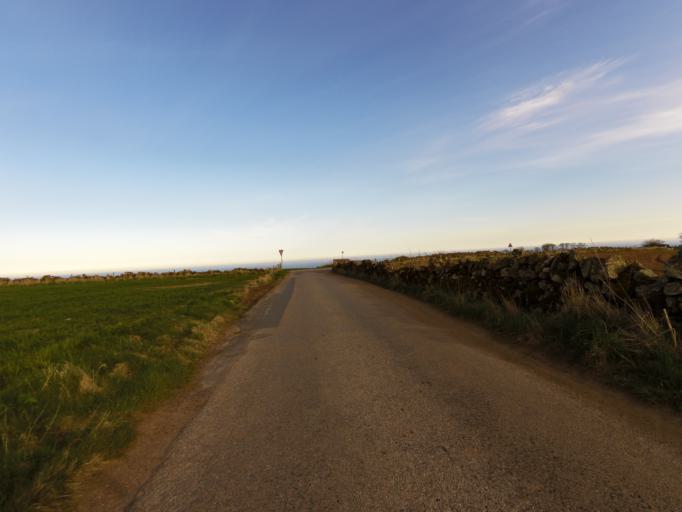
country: GB
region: Scotland
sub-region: Aberdeenshire
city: Stonehaven
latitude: 56.9105
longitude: -2.2136
